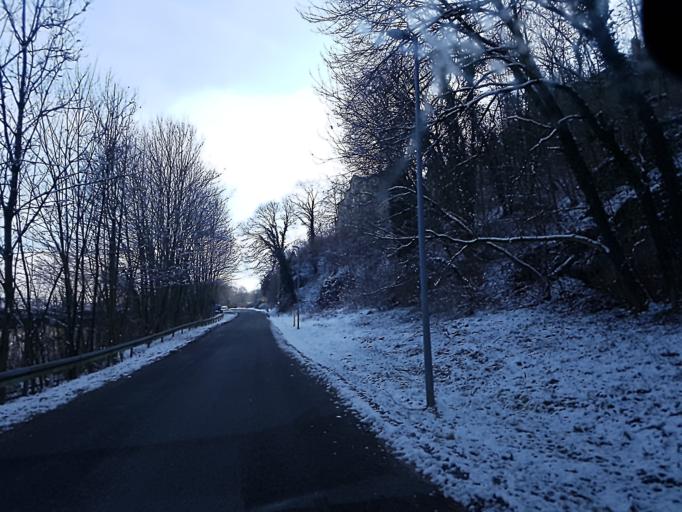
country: DE
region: Saxony
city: Leisnig
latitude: 51.1621
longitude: 12.9280
